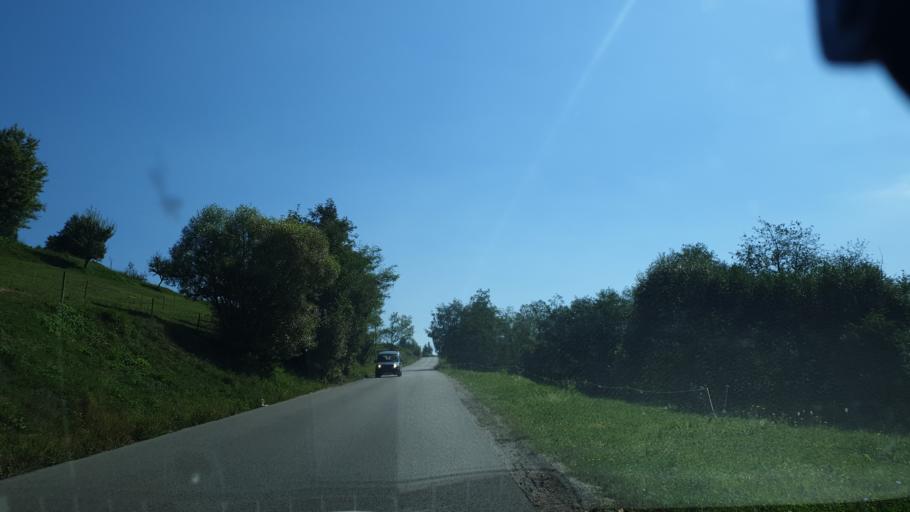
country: RS
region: Central Serbia
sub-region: Zlatiborski Okrug
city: Nova Varos
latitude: 43.4378
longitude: 19.8662
